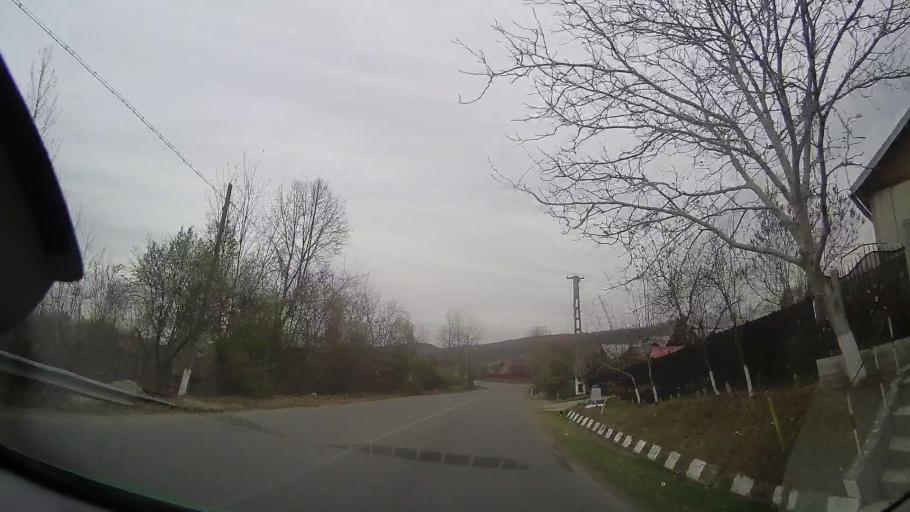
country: RO
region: Prahova
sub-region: Comuna Iordachianu
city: Iordacheanu
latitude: 45.0221
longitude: 26.2358
